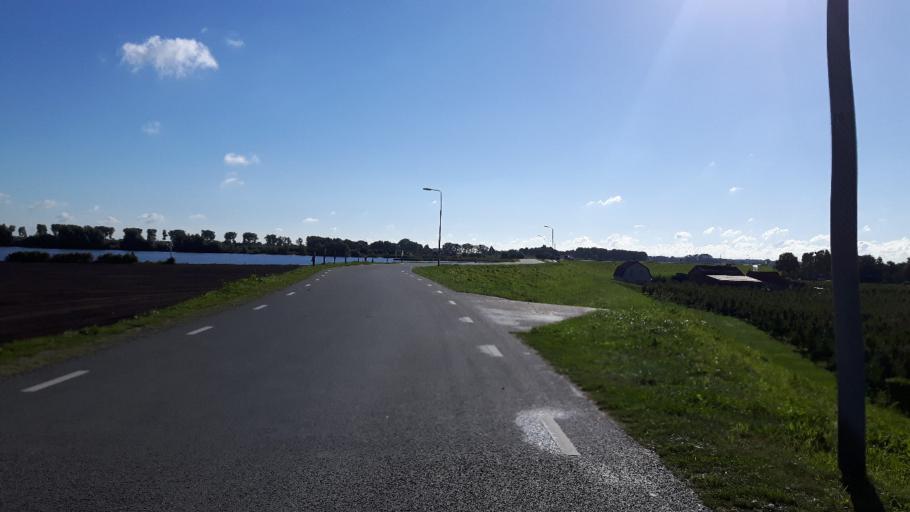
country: NL
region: Utrecht
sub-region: Gemeente Vianen
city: Vianen
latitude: 51.9832
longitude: 5.1372
